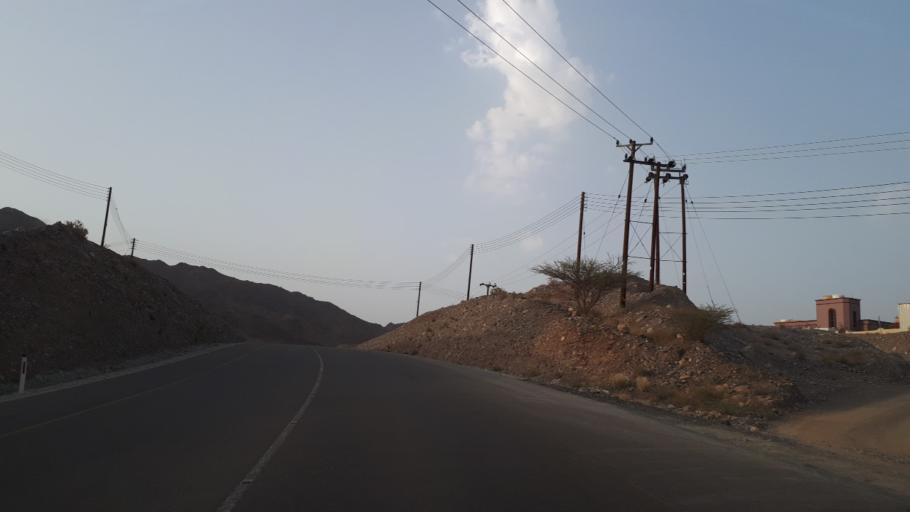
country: OM
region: Al Batinah
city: Rustaq
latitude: 23.3986
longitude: 57.2398
